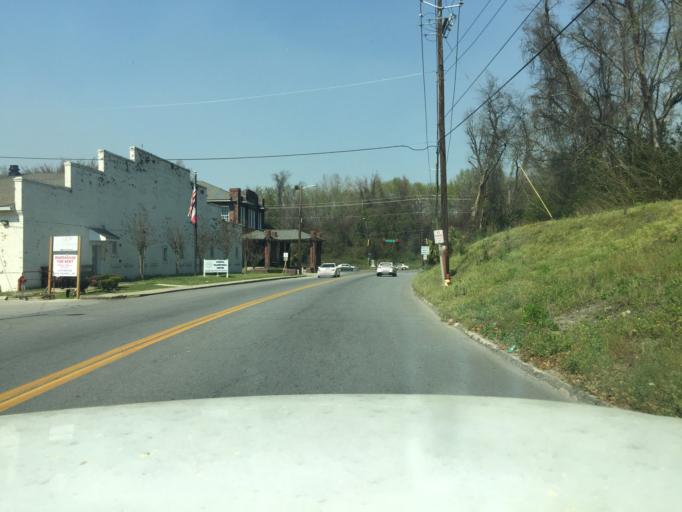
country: US
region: Georgia
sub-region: Chatham County
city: Savannah
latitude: 32.0779
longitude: -81.1110
